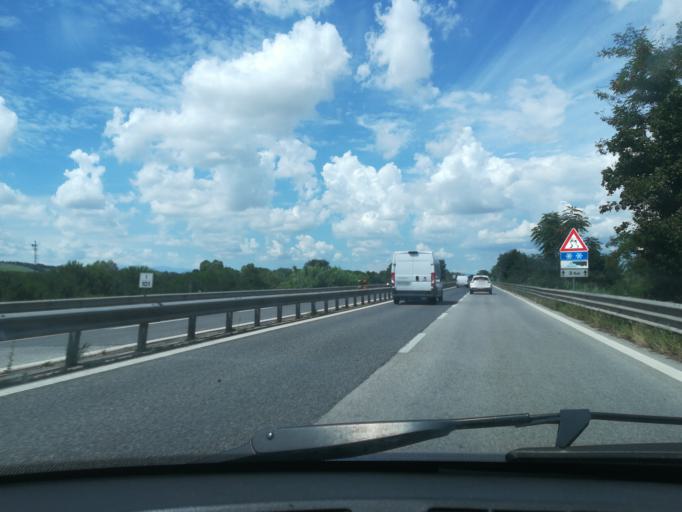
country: IT
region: The Marches
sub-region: Provincia di Macerata
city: Borgo Stazione
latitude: 43.2738
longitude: 13.6263
